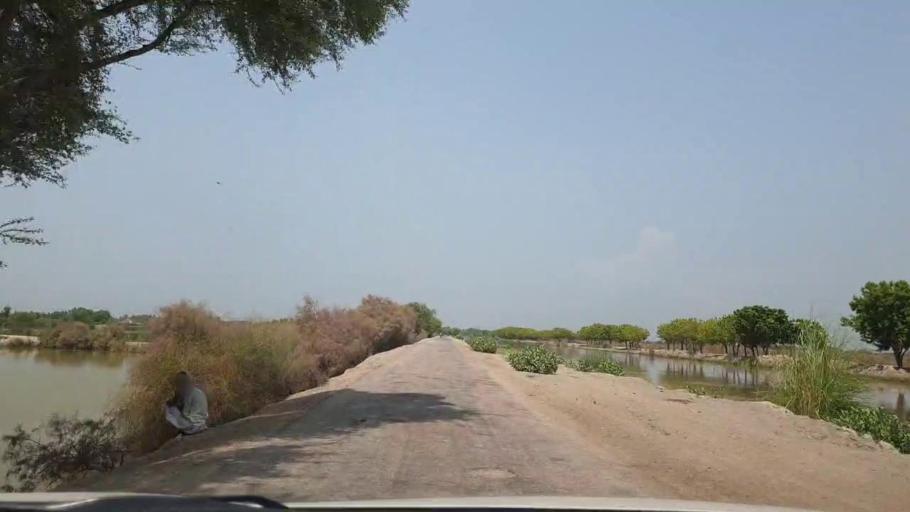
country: PK
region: Sindh
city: Dokri
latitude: 27.3489
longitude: 68.1121
